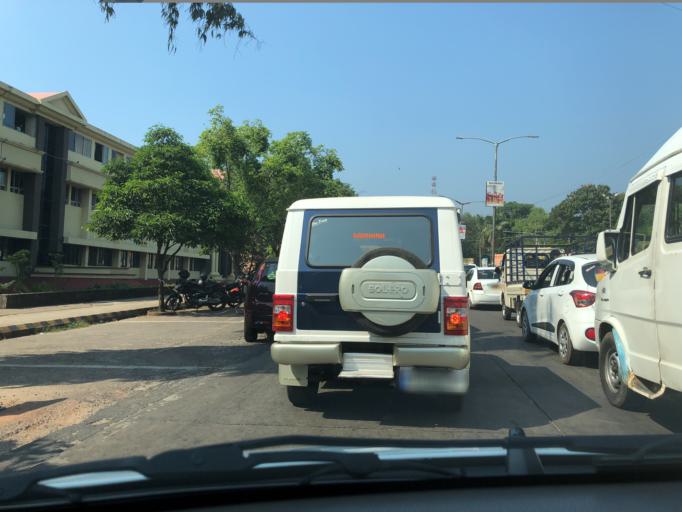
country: IN
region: Karnataka
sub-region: Dakshina Kannada
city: Mangalore
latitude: 12.8847
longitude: 74.8389
